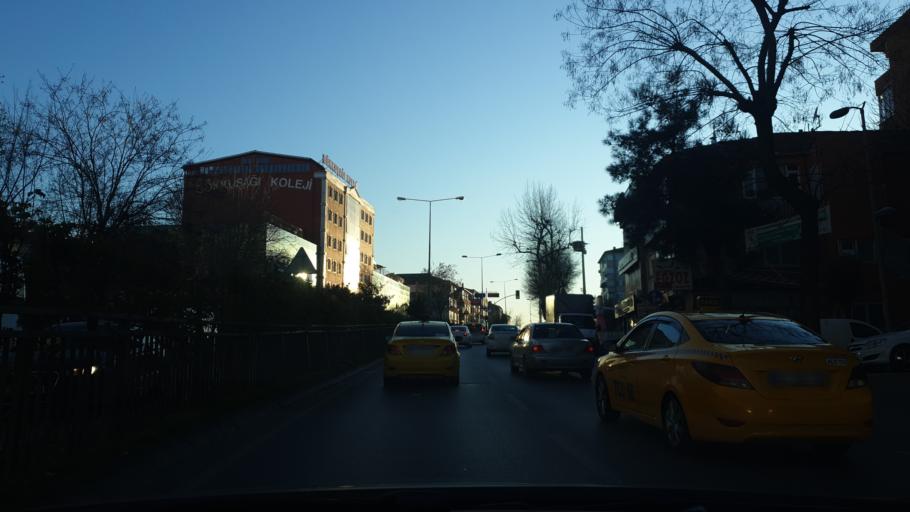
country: TR
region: Istanbul
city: merter keresteciler
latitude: 41.0078
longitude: 28.8742
